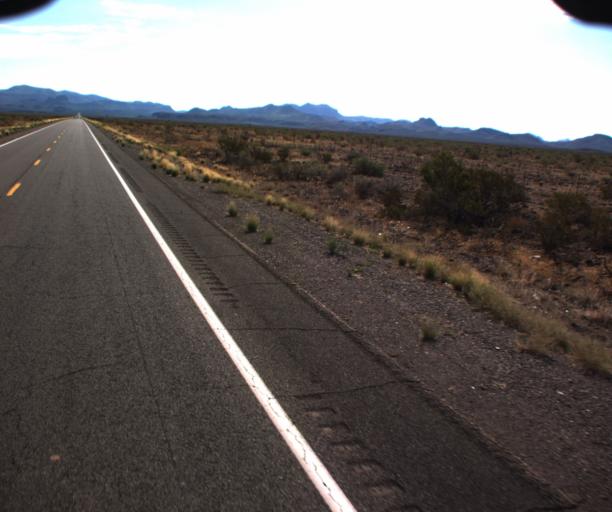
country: US
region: Arizona
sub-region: Graham County
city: Safford
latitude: 32.8168
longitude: -109.4862
